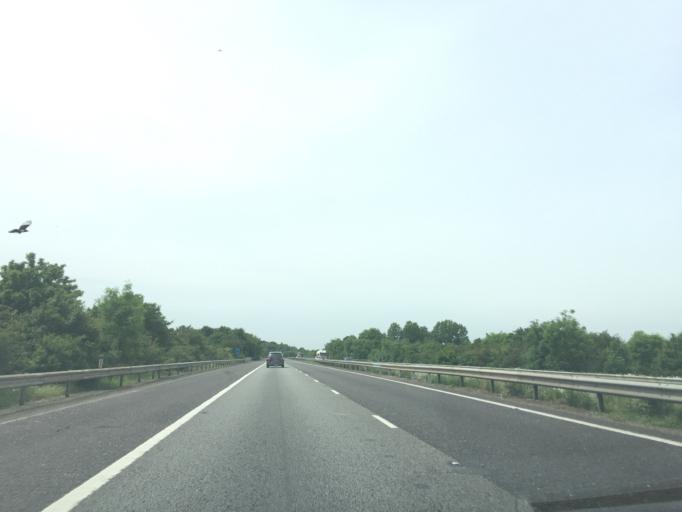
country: GB
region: England
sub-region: Kent
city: Borough Green
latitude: 51.3027
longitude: 0.3384
